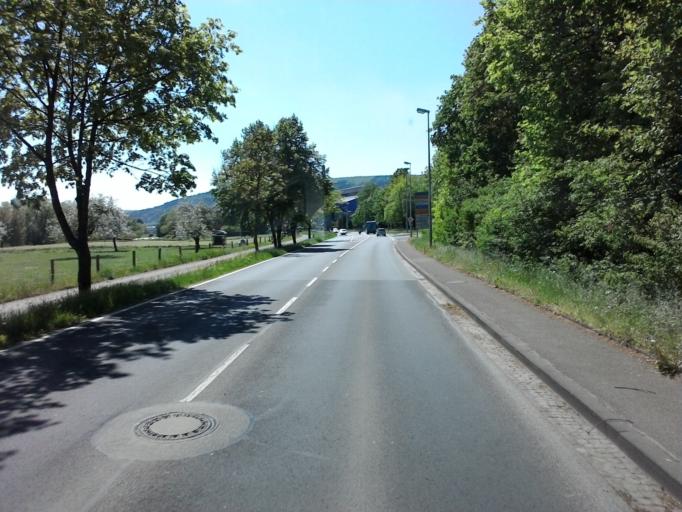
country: DE
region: Bavaria
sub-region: Regierungsbezirk Unterfranken
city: Lohr am Main
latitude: 49.9876
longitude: 9.5795
